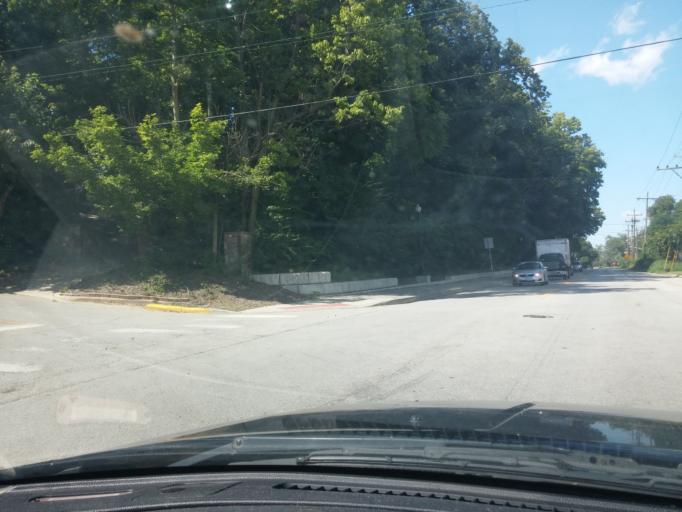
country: US
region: Indiana
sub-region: Tippecanoe County
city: West Lafayette
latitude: 40.4320
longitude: -86.8991
